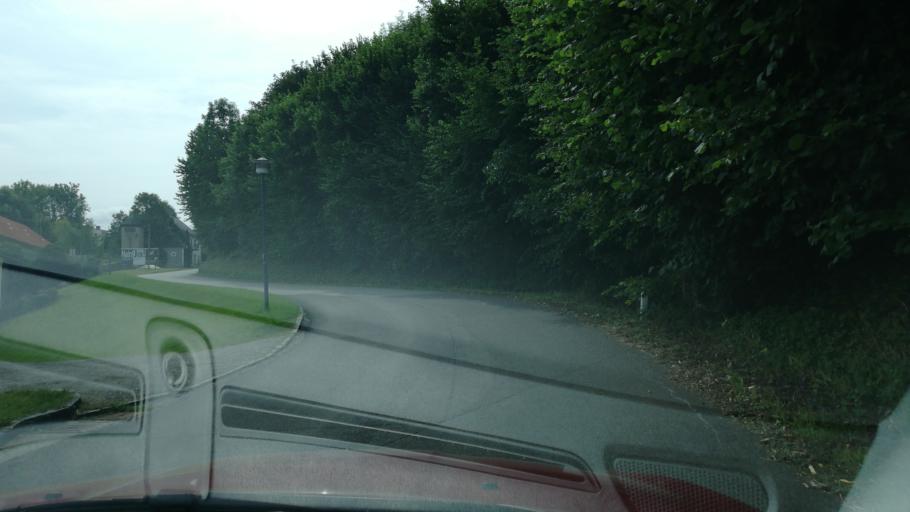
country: AT
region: Upper Austria
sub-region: Politischer Bezirk Rohrbach
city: Kleinzell im Muehlkreis
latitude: 48.4849
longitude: 13.9961
